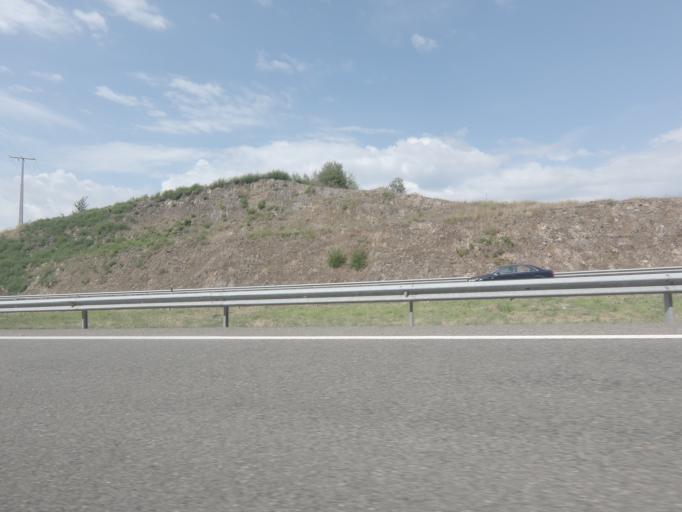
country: ES
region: Galicia
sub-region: Provincia de Ourense
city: Ourense
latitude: 42.3459
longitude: -7.8878
